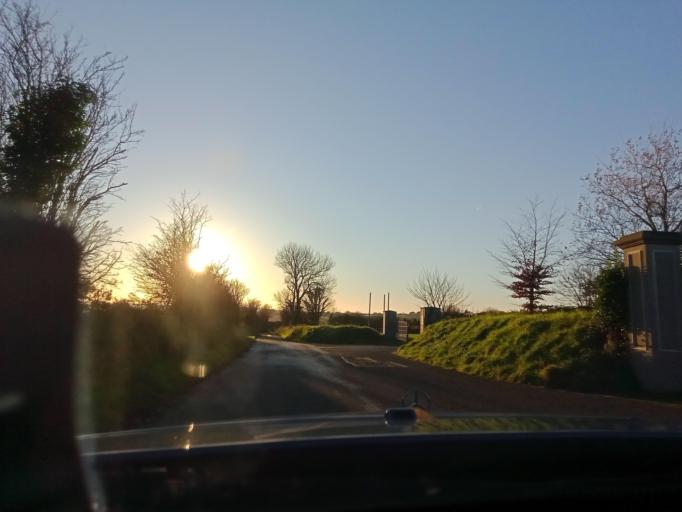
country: IE
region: Leinster
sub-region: Loch Garman
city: New Ross
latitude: 52.3781
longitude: -7.0115
